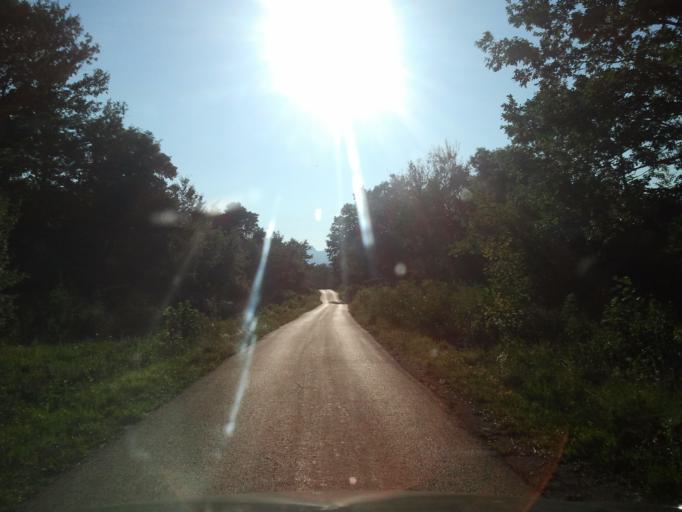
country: HR
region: Zadarska
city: Gracac
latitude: 44.3832
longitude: 15.7064
